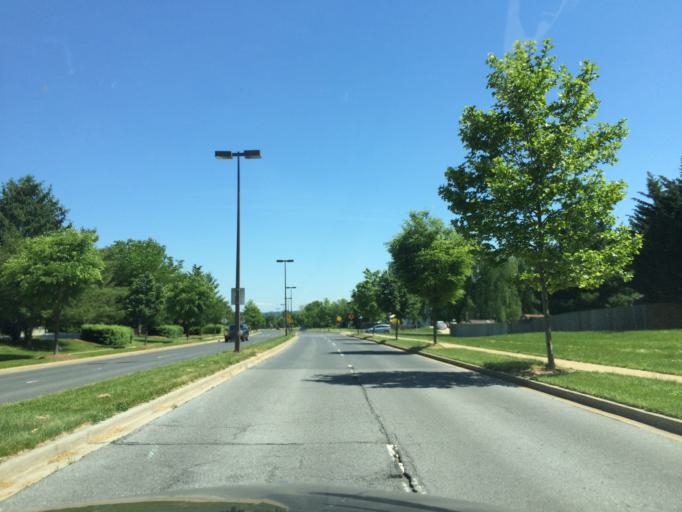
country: US
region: Maryland
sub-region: Frederick County
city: Frederick
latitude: 39.4365
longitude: -77.3930
